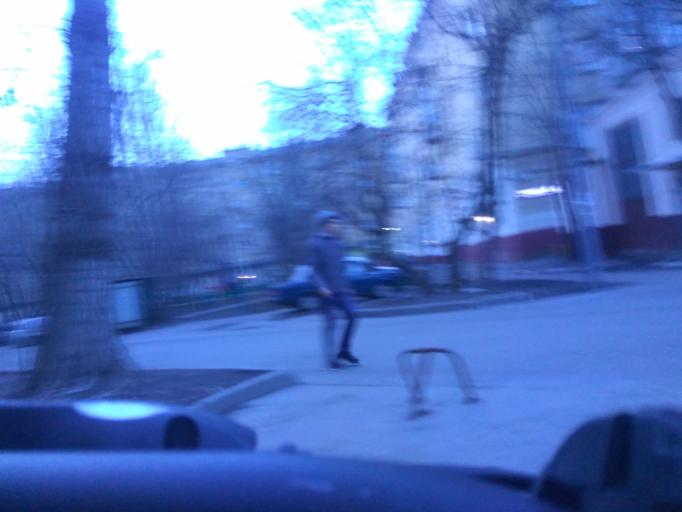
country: RU
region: Moskovskaya
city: Presnenskiy
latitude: 55.7395
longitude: 37.5449
